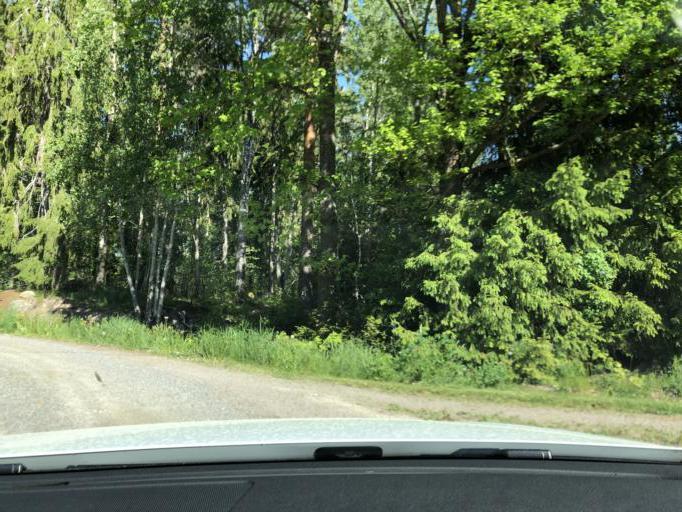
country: SE
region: Dalarna
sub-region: Avesta Kommun
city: Horndal
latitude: 60.2058
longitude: 16.4954
